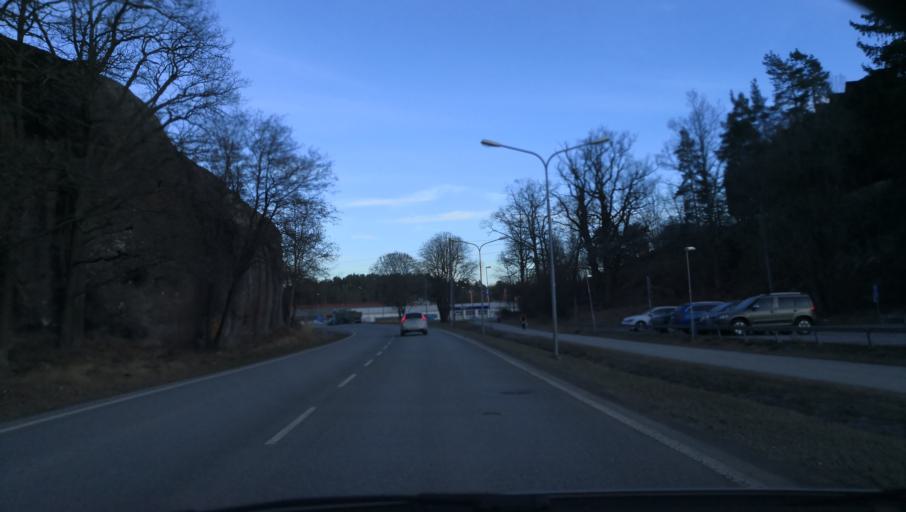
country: SE
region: Stockholm
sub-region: Varmdo Kommun
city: Gustavsberg
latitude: 59.3306
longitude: 18.3903
